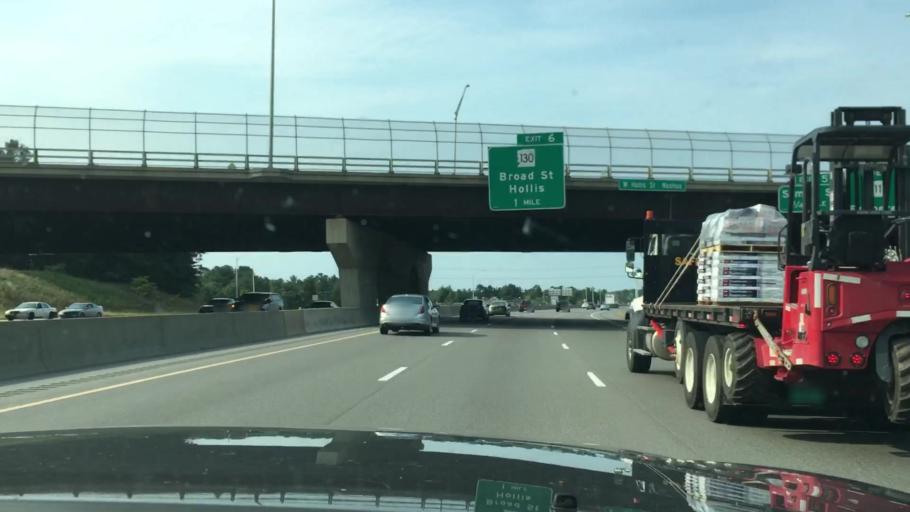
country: US
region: New Hampshire
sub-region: Hillsborough County
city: Nashua
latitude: 42.7464
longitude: -71.4923
